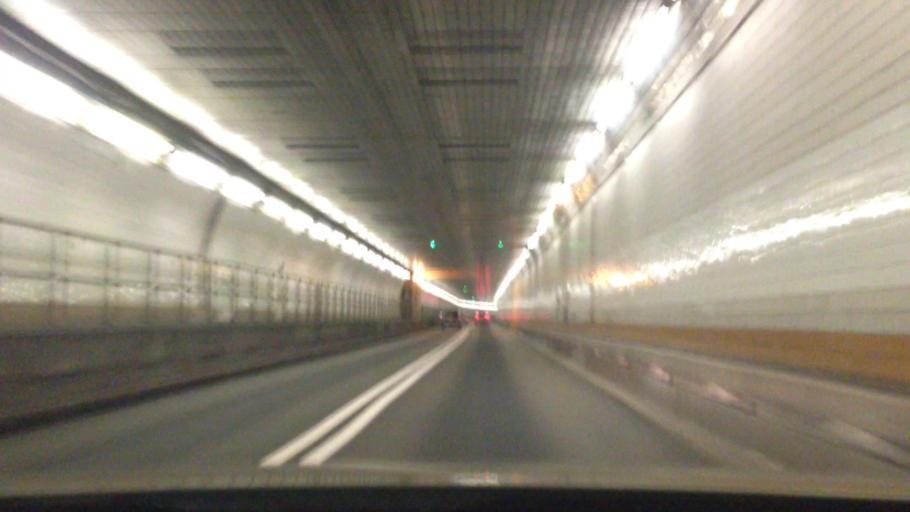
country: US
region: New York
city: New York City
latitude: 40.7253
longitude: -74.0158
